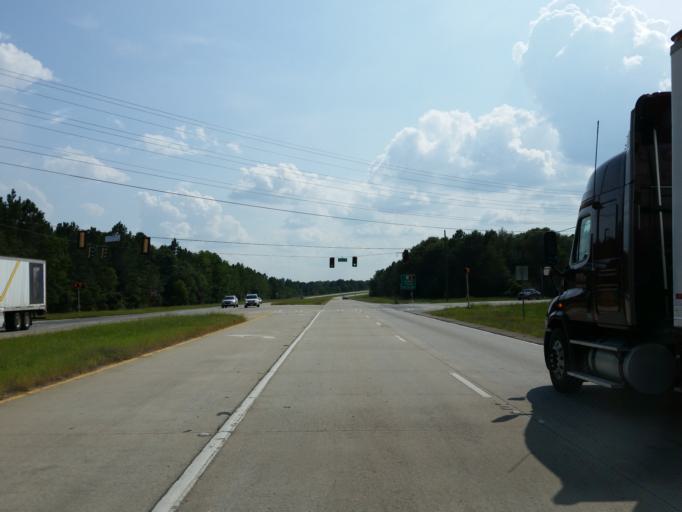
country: US
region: Georgia
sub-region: Crisp County
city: Cordele
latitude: 31.9269
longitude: -83.7598
